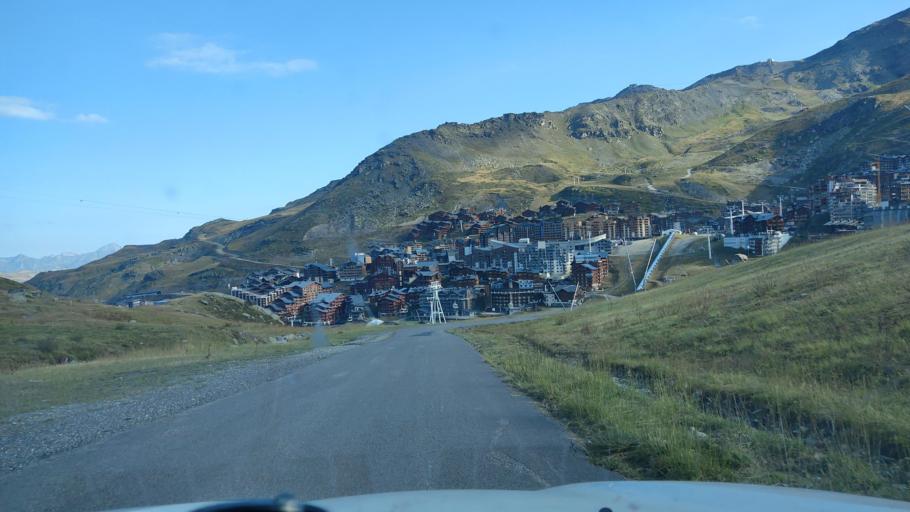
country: FR
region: Rhone-Alpes
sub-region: Departement de la Savoie
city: Val Thorens
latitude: 45.2917
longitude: 6.5820
